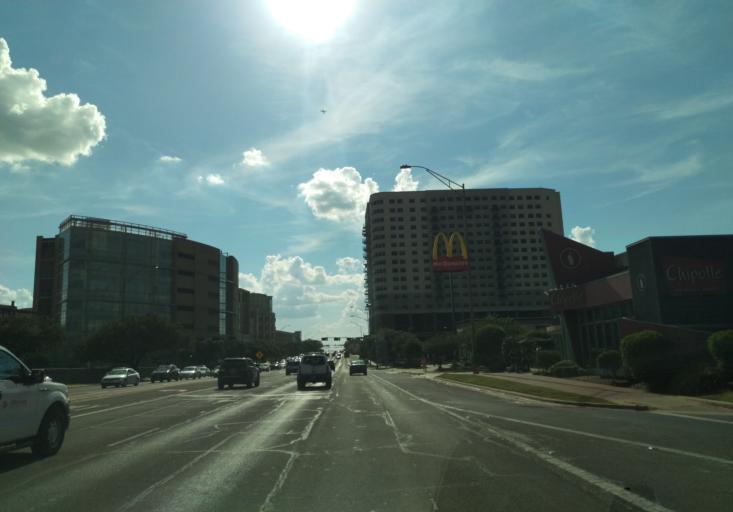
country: US
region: Texas
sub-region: Brazos County
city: College Station
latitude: 30.6225
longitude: -96.3410
